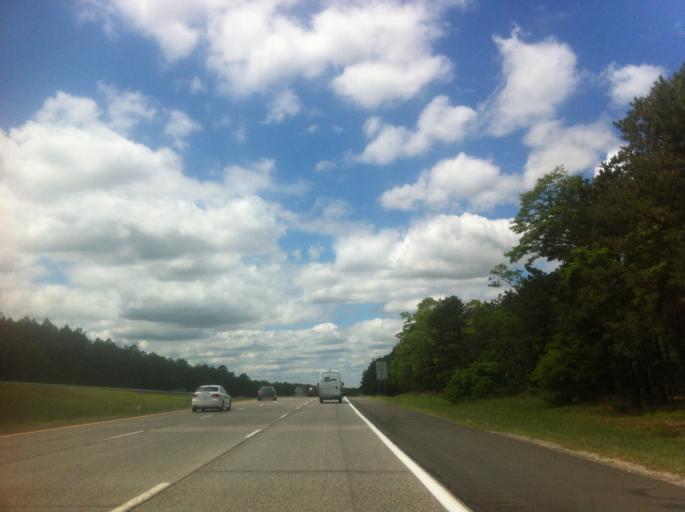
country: US
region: New York
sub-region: Suffolk County
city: Manorville
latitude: 40.8804
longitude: -72.7721
